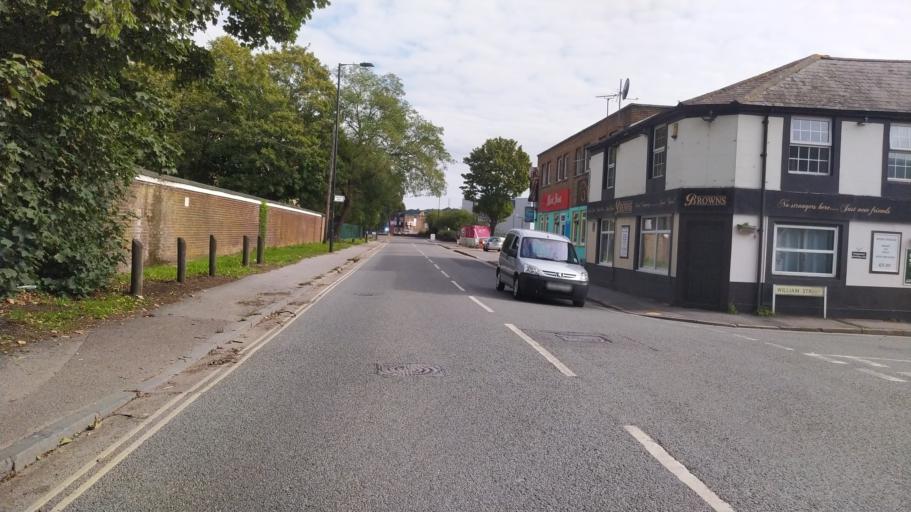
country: GB
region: England
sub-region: Southampton
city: Southampton
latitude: 50.9104
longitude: -1.3852
